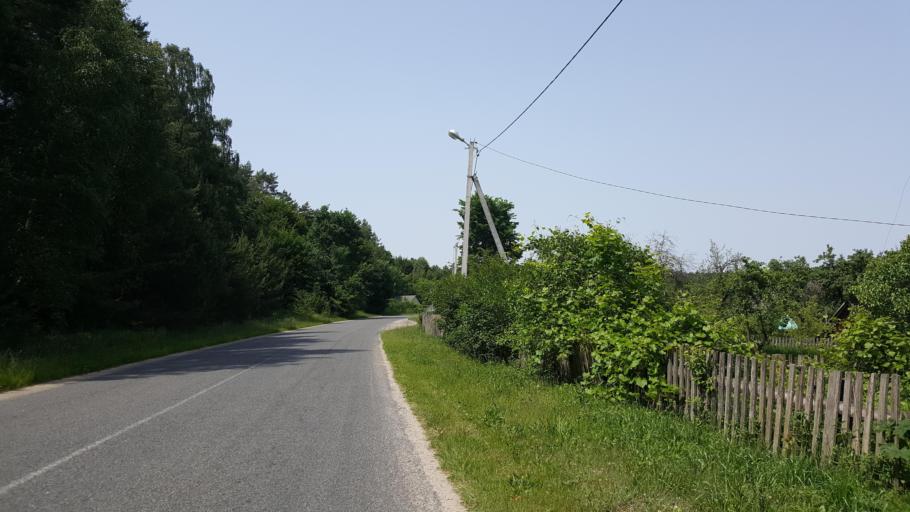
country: BY
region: Brest
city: Kamyanyuki
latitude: 52.5076
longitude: 23.8545
